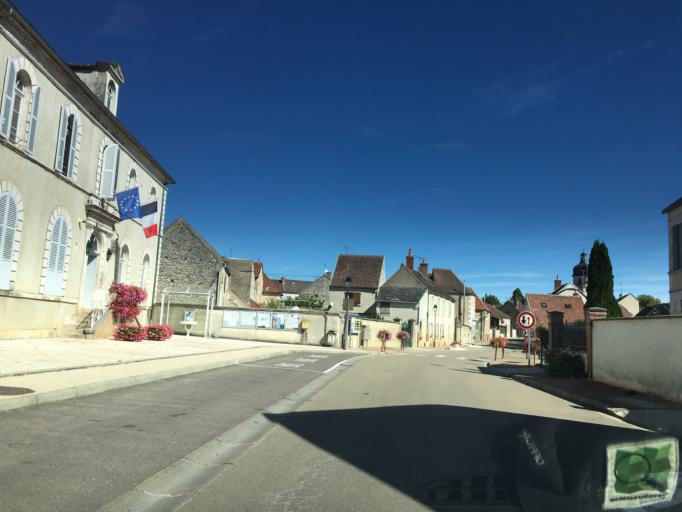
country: FR
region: Bourgogne
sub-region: Departement de l'Yonne
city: Vermenton
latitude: 47.6589
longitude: 3.6625
